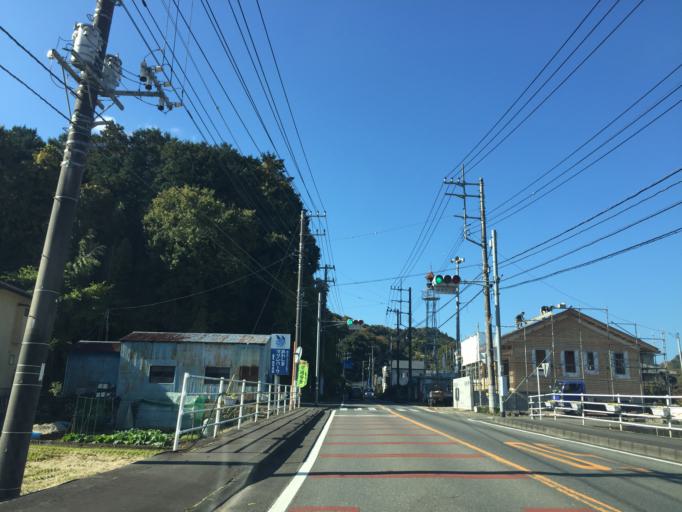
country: JP
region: Shizuoka
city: Mishima
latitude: 35.0218
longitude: 138.9336
